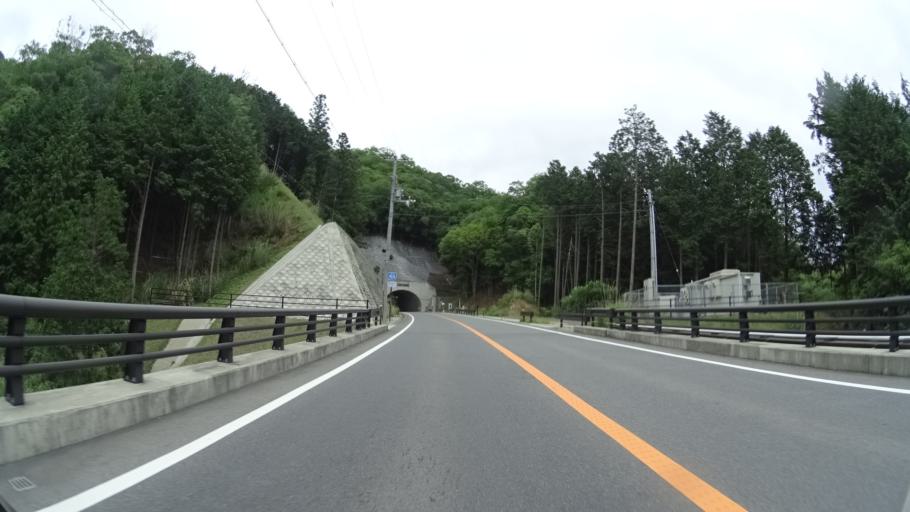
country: JP
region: Mie
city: Ueno-ebisumachi
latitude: 34.7701
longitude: 135.9802
